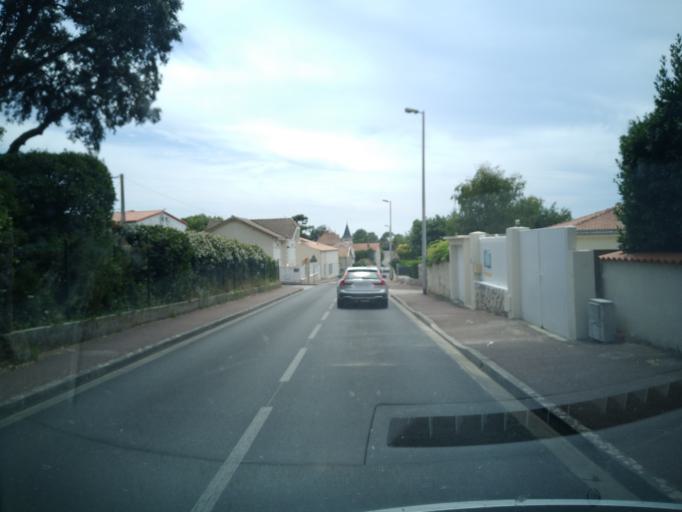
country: FR
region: Poitou-Charentes
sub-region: Departement de la Charente-Maritime
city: Saint-Palais-sur-Mer
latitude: 45.6452
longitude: -1.0847
